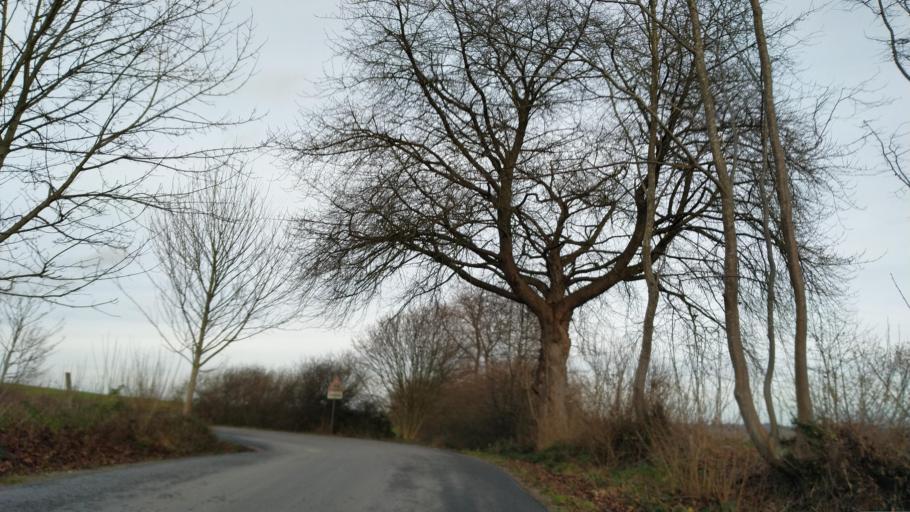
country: DE
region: Schleswig-Holstein
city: Malente
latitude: 54.1946
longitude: 10.6070
